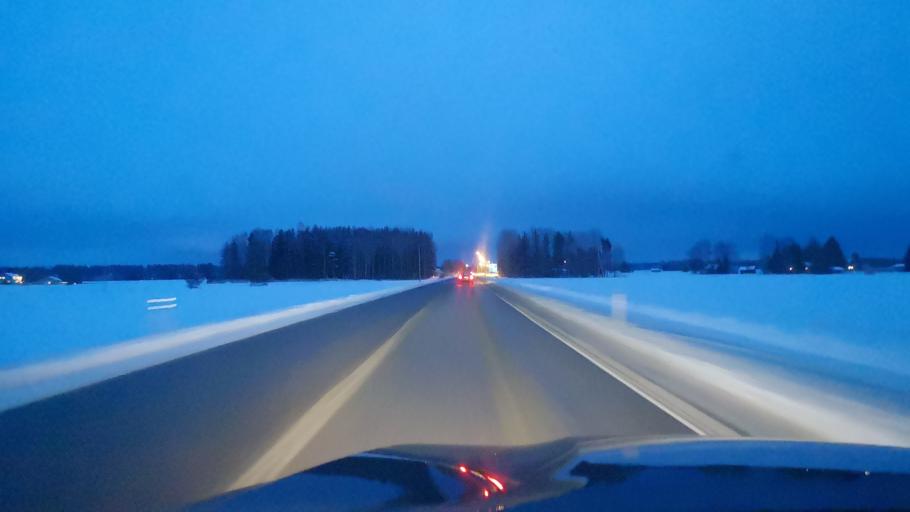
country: FI
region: Varsinais-Suomi
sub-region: Loimaa
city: Loimaa
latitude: 60.8815
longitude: 23.0810
